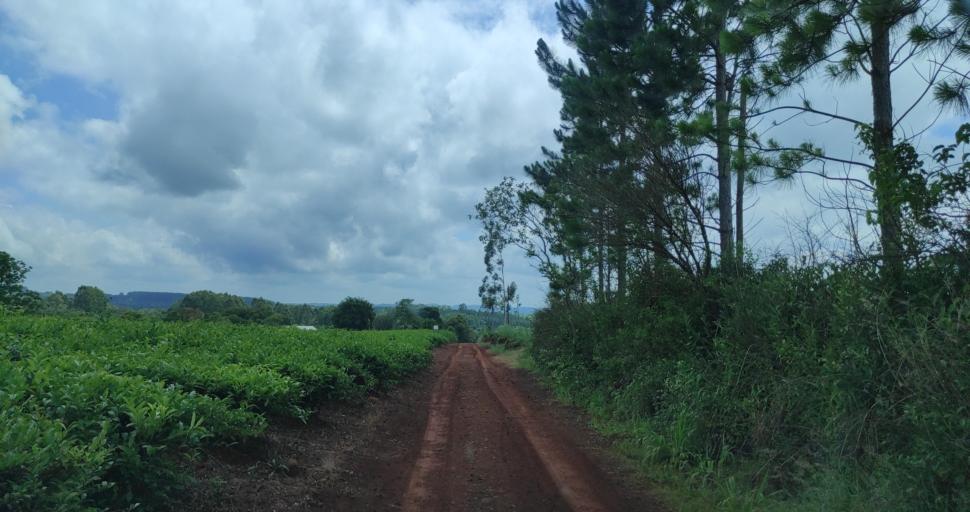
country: AR
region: Misiones
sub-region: Departamento de Veinticinco de Mayo
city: Veinticinco de Mayo
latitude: -27.4166
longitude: -54.7293
